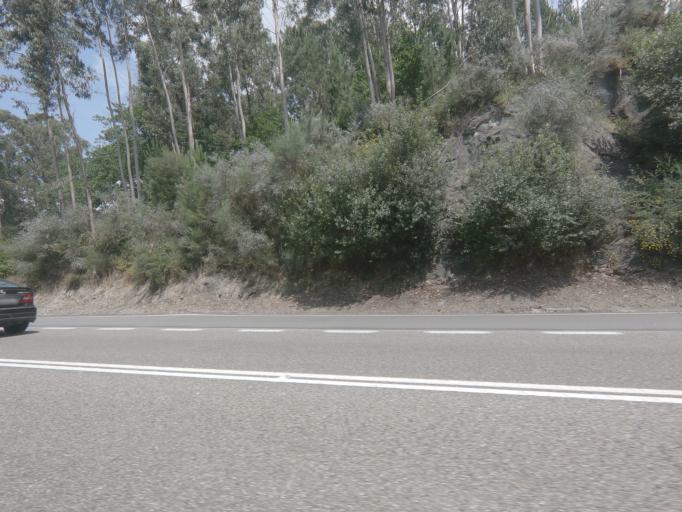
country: ES
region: Galicia
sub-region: Provincia de Pontevedra
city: Tomino
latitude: 42.0445
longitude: -8.7283
